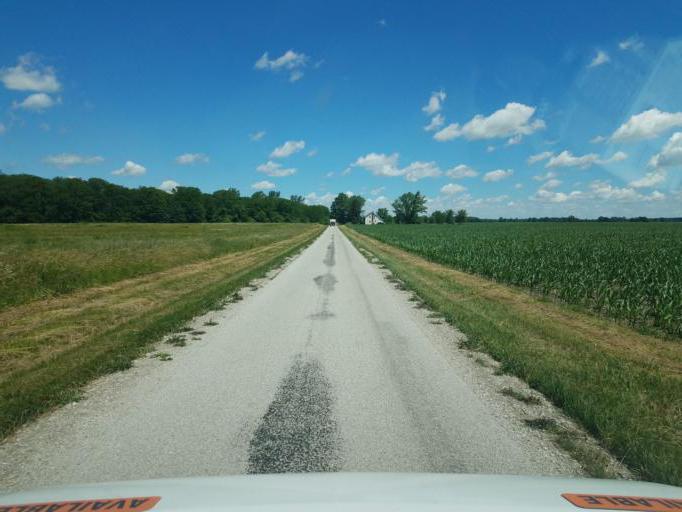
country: US
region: Ohio
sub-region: Crawford County
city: Bucyrus
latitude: 40.6914
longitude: -82.9389
